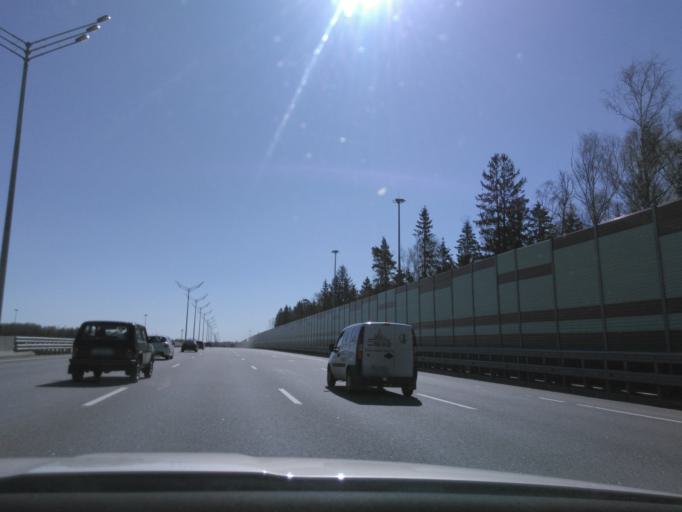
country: RU
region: Moskovskaya
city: Novopodrezkovo
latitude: 55.9590
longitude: 37.4050
